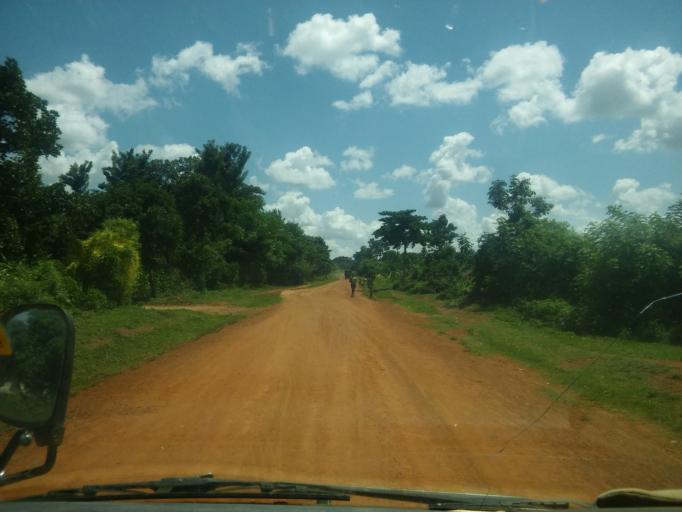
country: UG
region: Eastern Region
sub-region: Budaka District
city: Budaka
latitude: 1.1124
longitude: 33.9553
